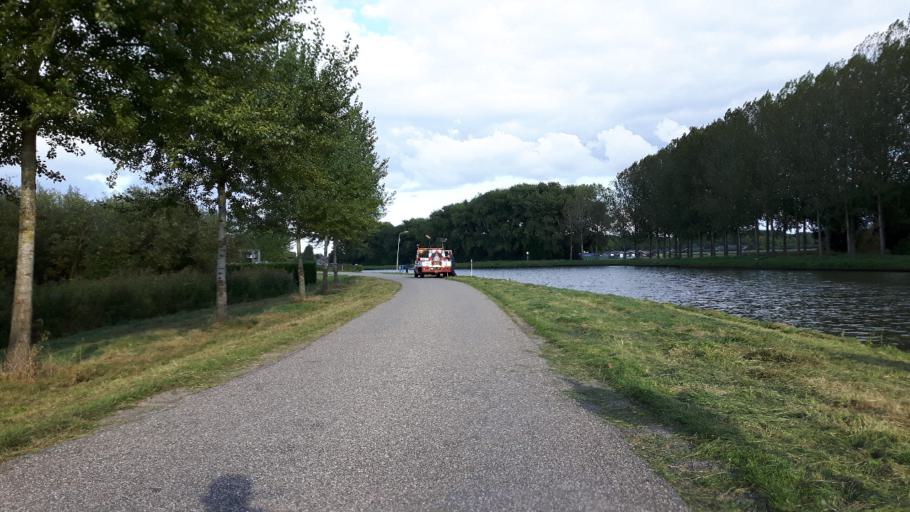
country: NL
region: Utrecht
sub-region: Gemeente Vianen
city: Vianen
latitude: 51.9713
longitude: 5.0769
